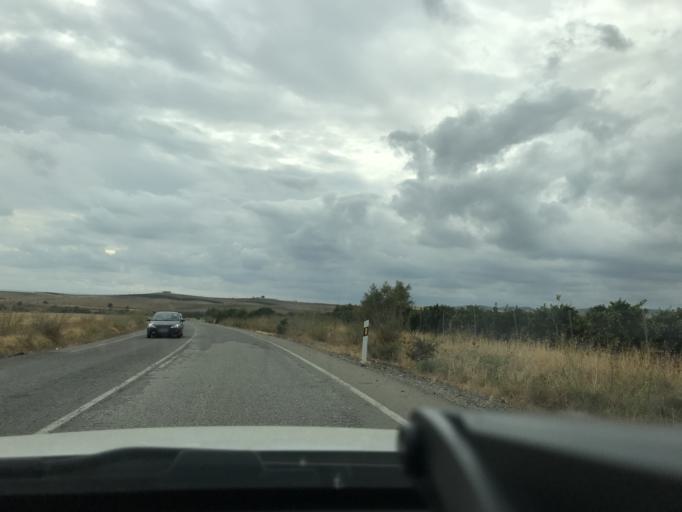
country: ES
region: Andalusia
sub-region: Provincia de Sevilla
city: Cantillana
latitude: 37.6266
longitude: -5.7823
